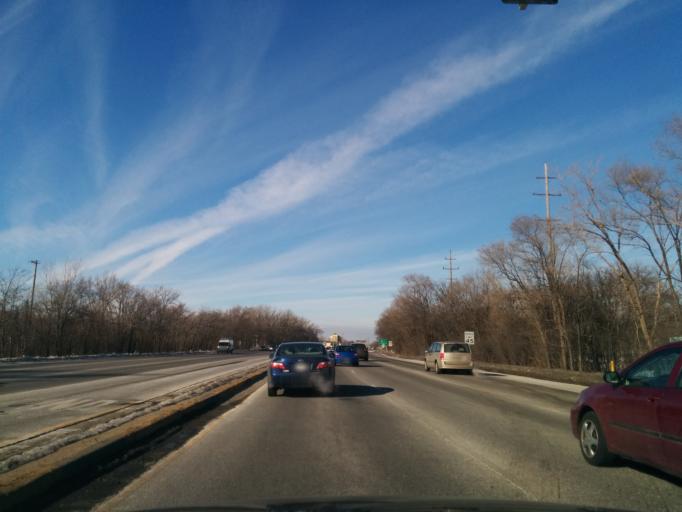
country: US
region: Illinois
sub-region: DuPage County
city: Elmhurst
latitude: 41.8998
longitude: -87.9644
